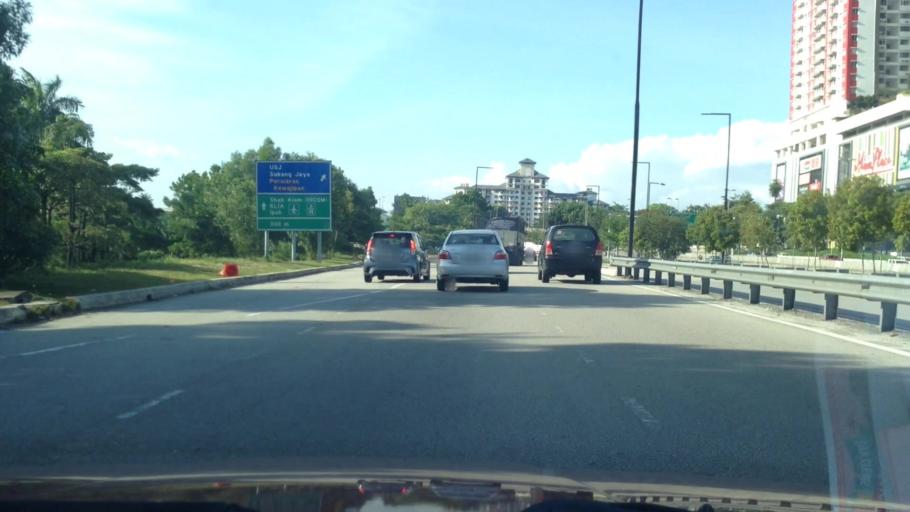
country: MY
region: Selangor
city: Subang Jaya
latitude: 3.0244
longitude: 101.5801
